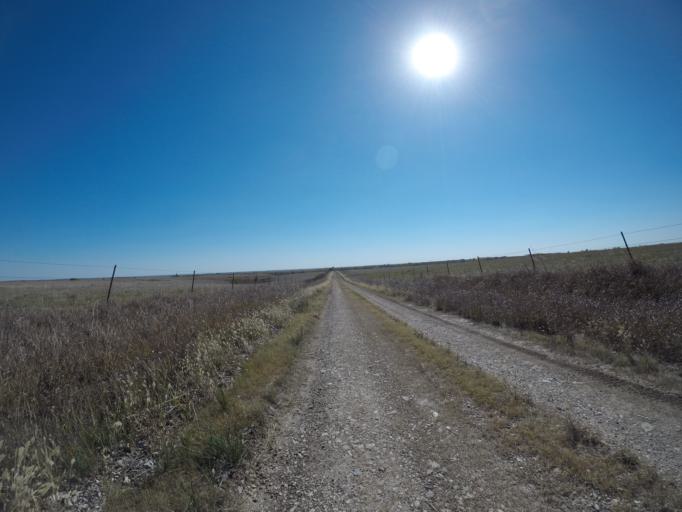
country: US
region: Kansas
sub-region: Wabaunsee County
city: Alma
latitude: 38.9901
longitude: -96.4642
